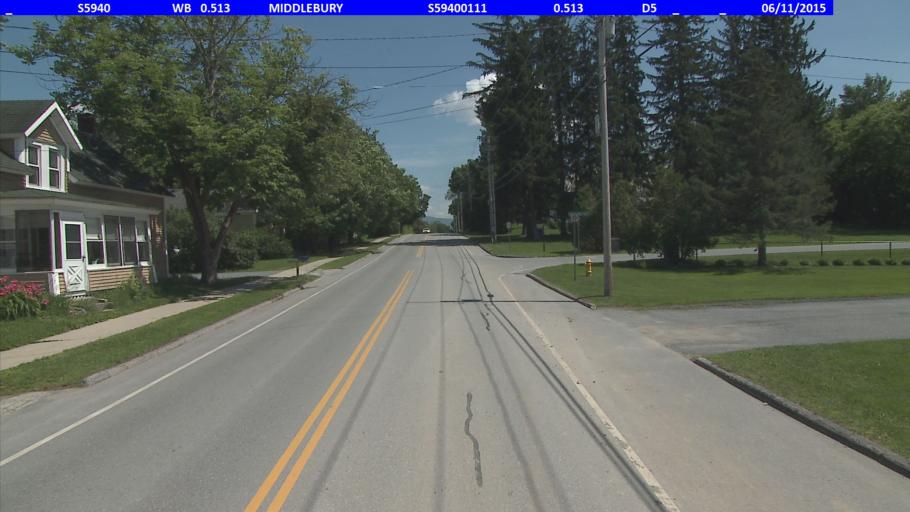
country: US
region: Vermont
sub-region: Addison County
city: Middlebury (village)
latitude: 44.0169
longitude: -73.1783
